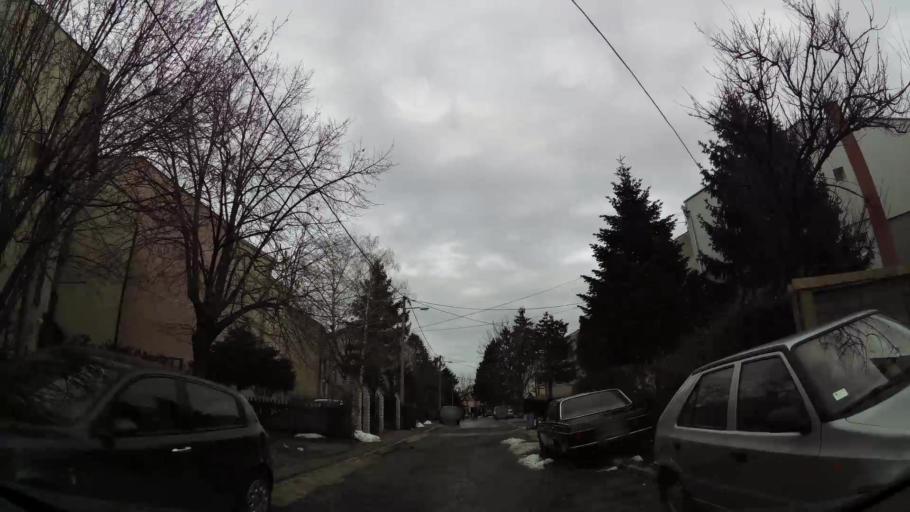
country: RS
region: Central Serbia
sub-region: Belgrade
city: Cukarica
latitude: 44.7611
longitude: 20.4094
